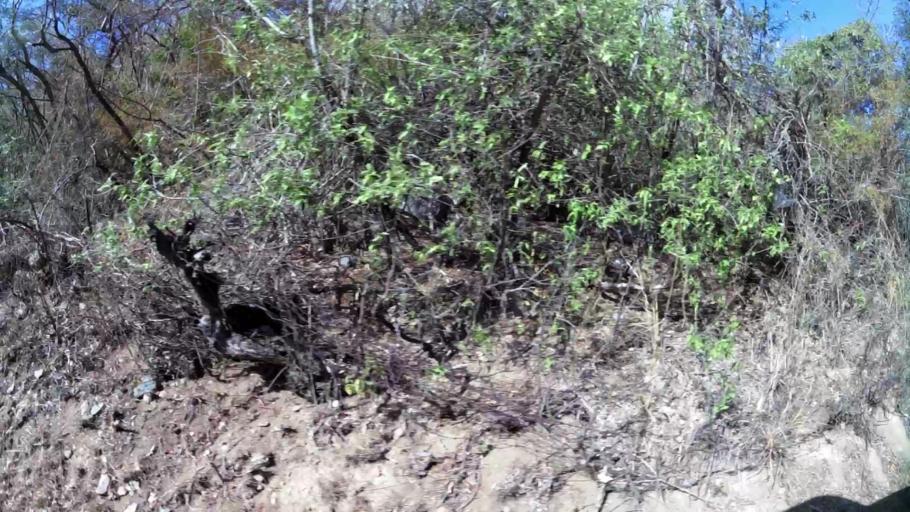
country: VG
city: Road Town
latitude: 18.3904
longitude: -64.6785
